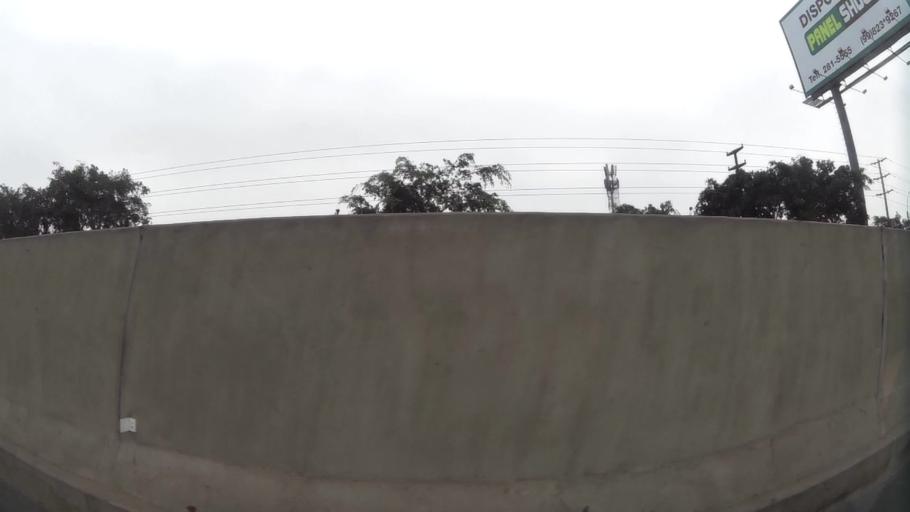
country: PE
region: Lima
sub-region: Lima
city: Independencia
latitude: -11.9847
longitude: -77.0649
